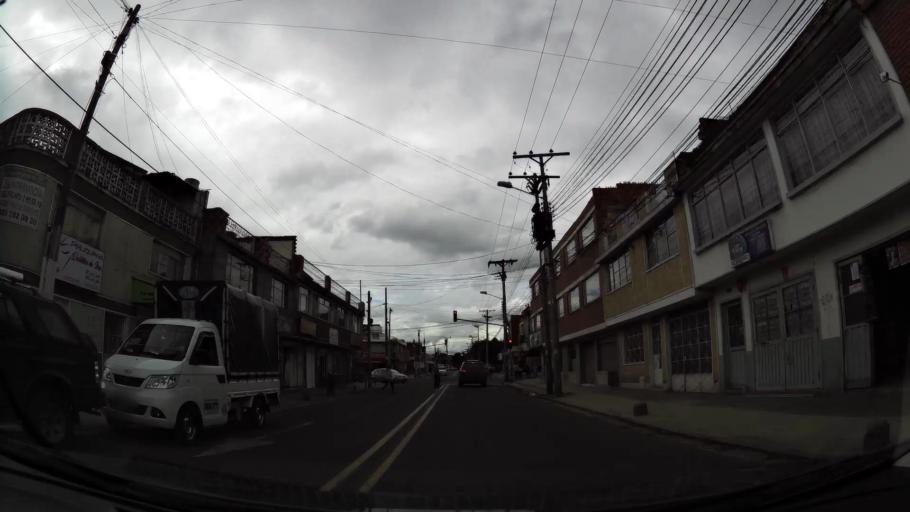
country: CO
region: Bogota D.C.
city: Bogota
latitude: 4.6724
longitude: -74.0948
